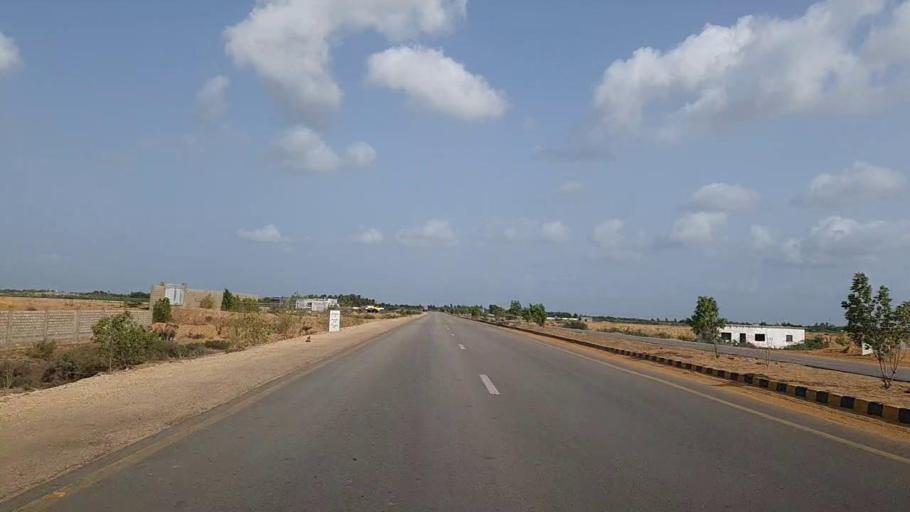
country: PK
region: Sindh
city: Gharo
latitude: 24.7340
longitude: 67.6015
